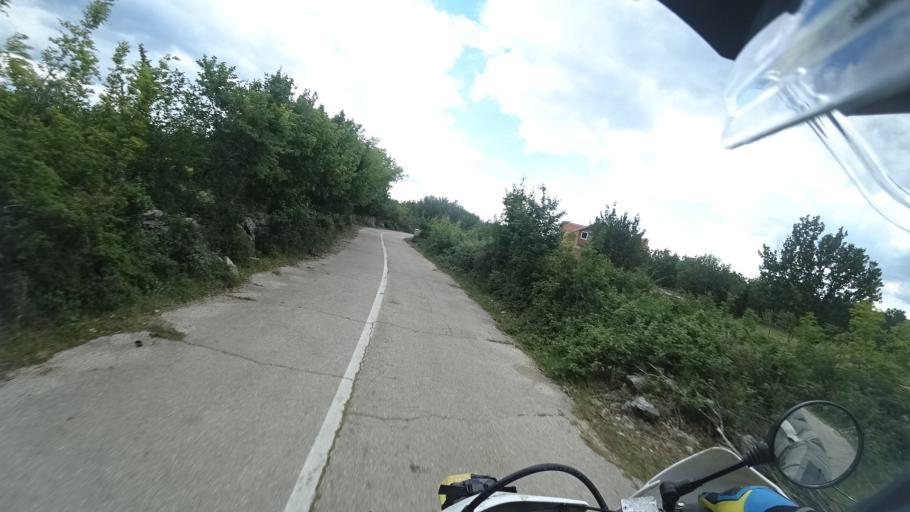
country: HR
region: Zadarska
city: Gracac
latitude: 44.1898
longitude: 15.9069
